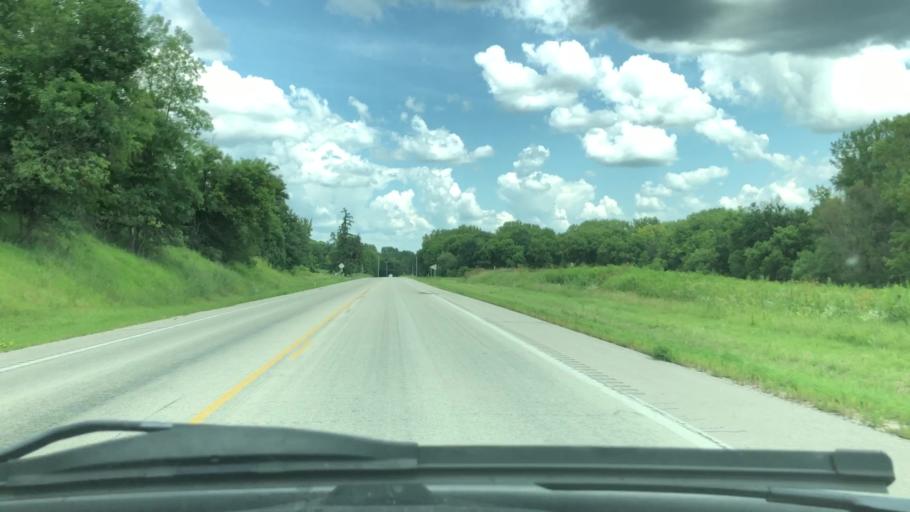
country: US
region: Minnesota
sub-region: Olmsted County
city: Rochester
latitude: 43.9839
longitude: -92.5079
